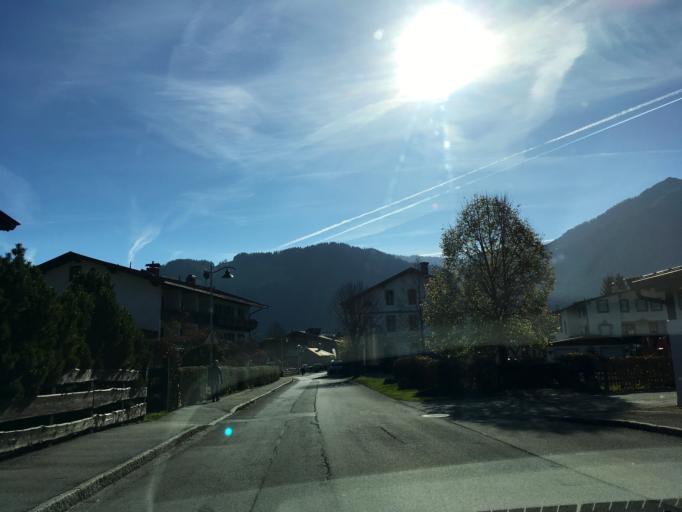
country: AT
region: Tyrol
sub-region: Politischer Bezirk Kufstein
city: Walchsee
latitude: 47.6534
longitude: 12.3170
